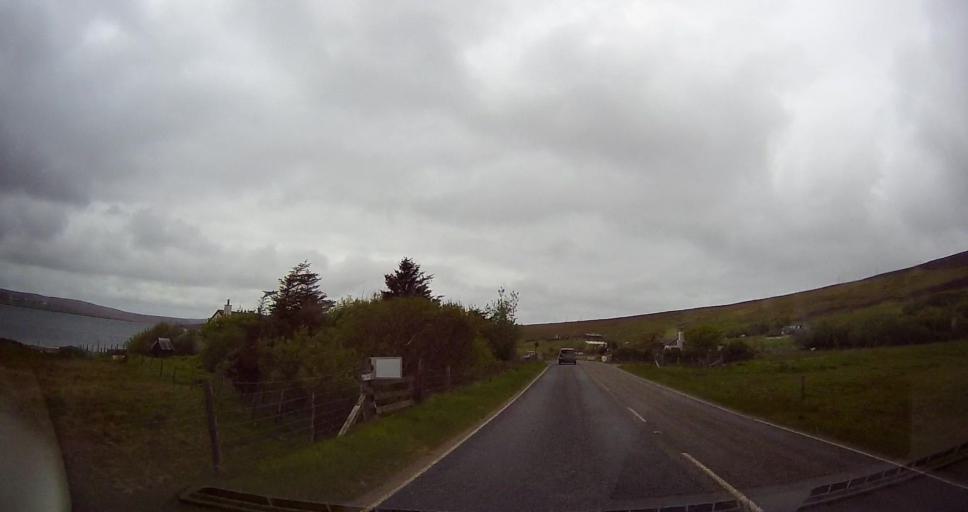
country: GB
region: Scotland
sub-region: Shetland Islands
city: Lerwick
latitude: 60.2446
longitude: -1.3532
